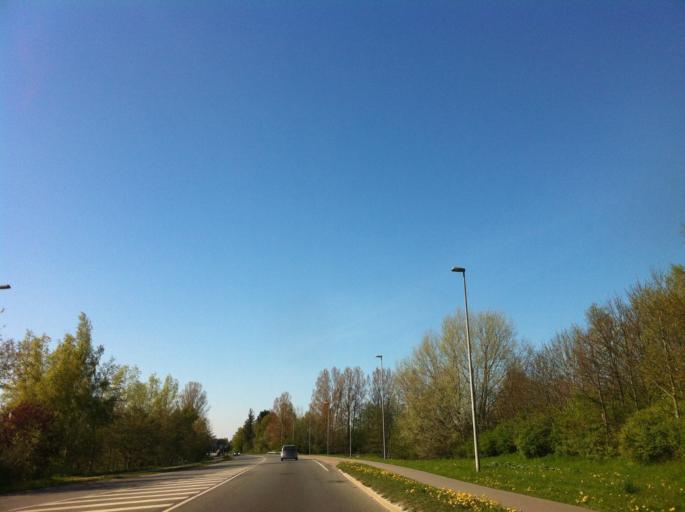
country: DK
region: Zealand
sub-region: Naestved Kommune
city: Naestved
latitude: 55.2402
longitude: 11.7782
